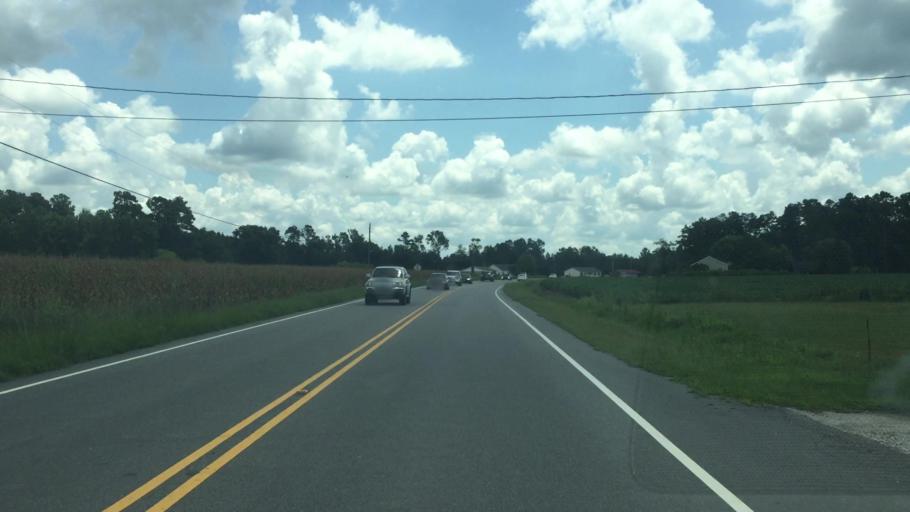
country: US
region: North Carolina
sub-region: Columbus County
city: Chadbourn
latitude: 34.2774
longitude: -78.8146
